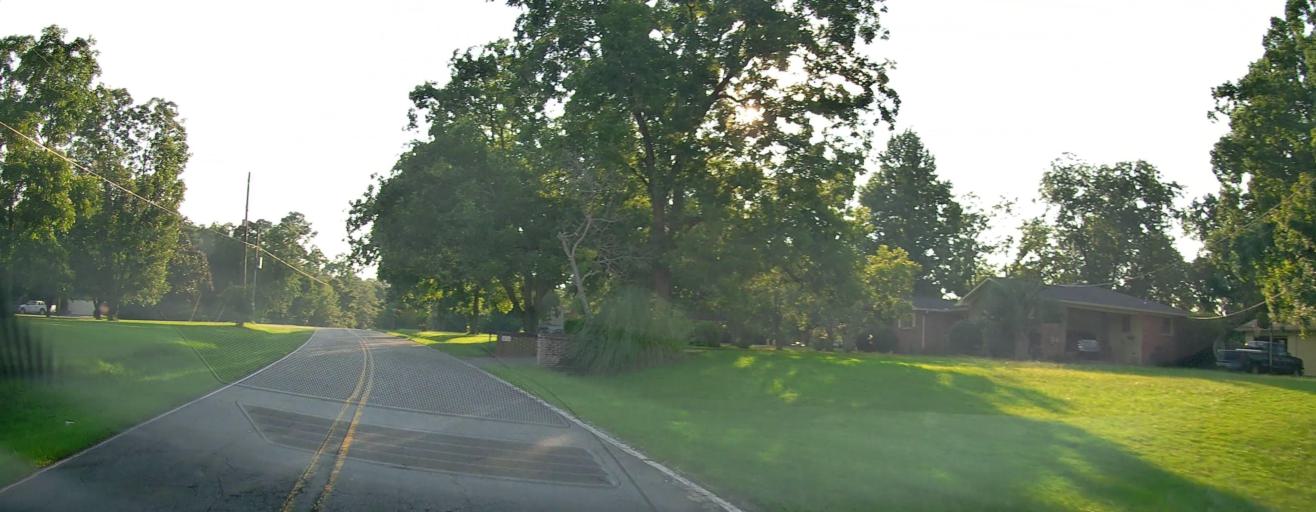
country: US
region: Georgia
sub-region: Peach County
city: Byron
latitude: 32.7294
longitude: -83.7467
